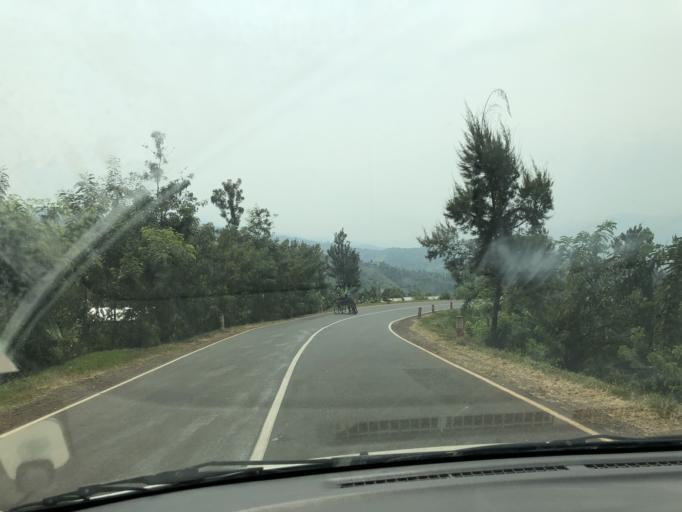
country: RW
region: Western Province
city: Cyangugu
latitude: -2.6705
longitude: 28.9946
